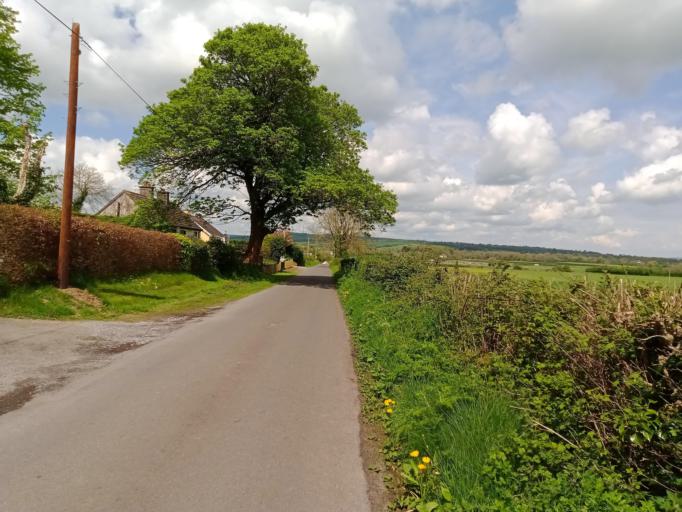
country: IE
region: Leinster
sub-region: Kilkenny
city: Ballyragget
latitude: 52.7303
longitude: -7.4179
